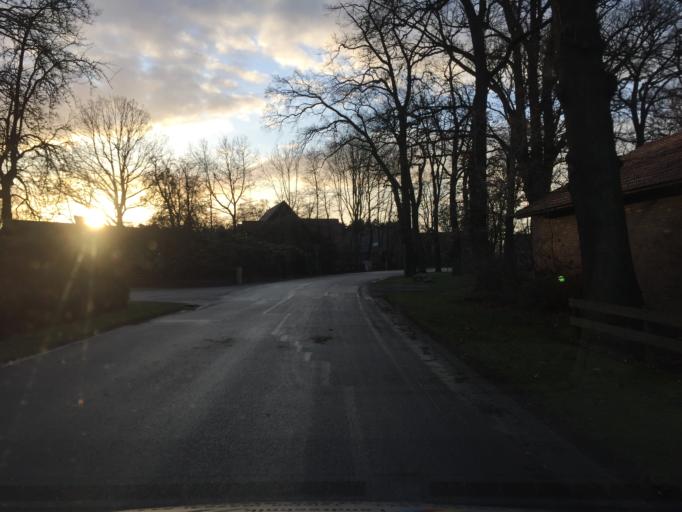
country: DE
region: Lower Saxony
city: Raddestorf
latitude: 52.4226
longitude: 8.9374
